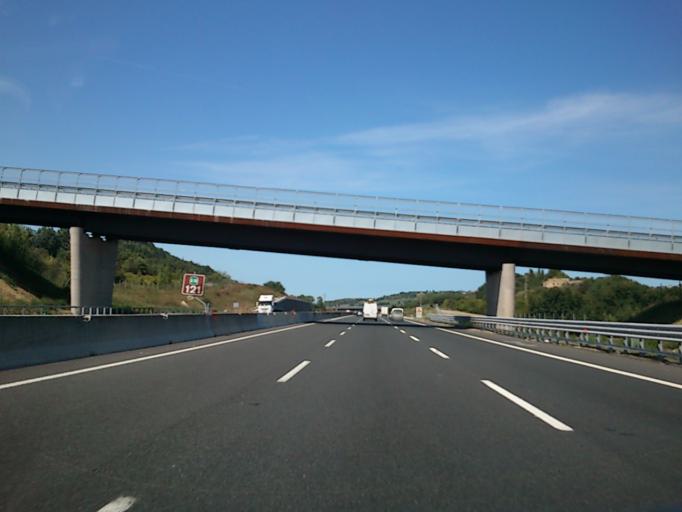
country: IT
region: The Marches
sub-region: Provincia di Pesaro e Urbino
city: Gradara
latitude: 43.9353
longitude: 12.7867
